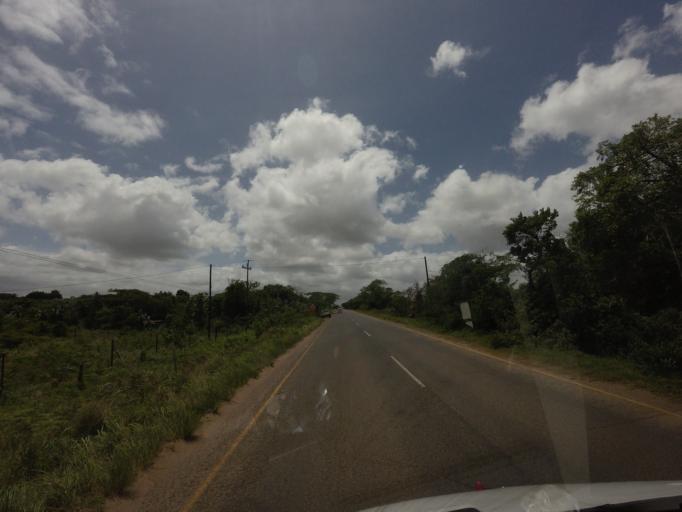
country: ZA
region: KwaZulu-Natal
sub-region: uMkhanyakude District Municipality
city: Mtubatuba
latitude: -28.3806
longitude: 32.3621
